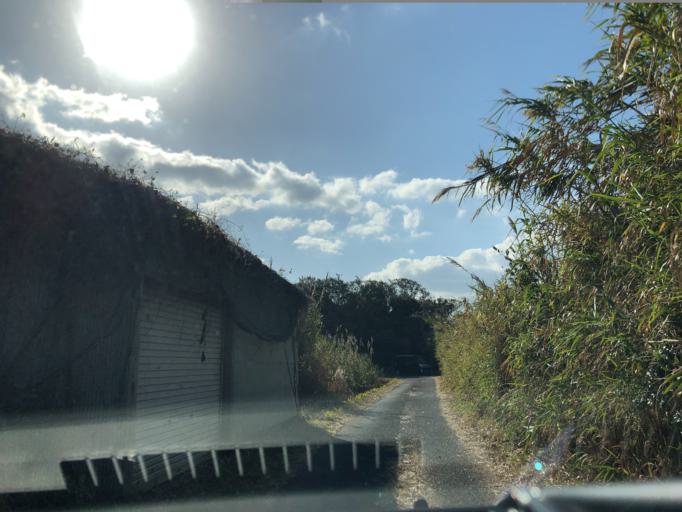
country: JP
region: Kochi
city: Sukumo
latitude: 32.9111
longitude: 132.6951
